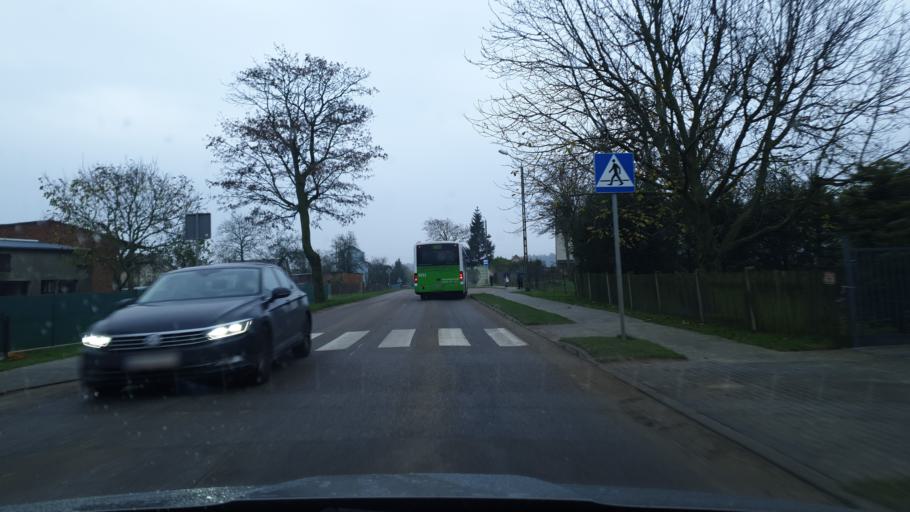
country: PL
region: Pomeranian Voivodeship
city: Strzelno
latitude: 54.7443
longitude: 18.3007
